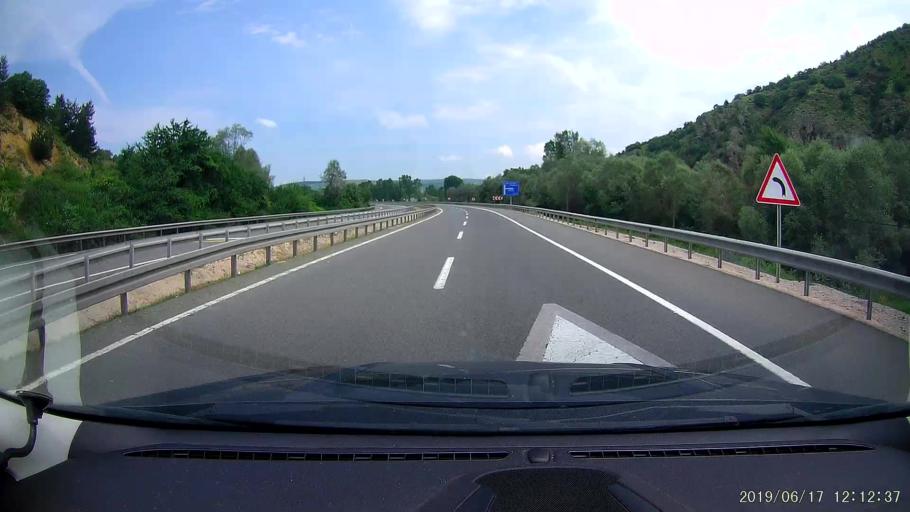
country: TR
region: Karabuk
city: Gozyeri
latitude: 40.8592
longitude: 32.6364
